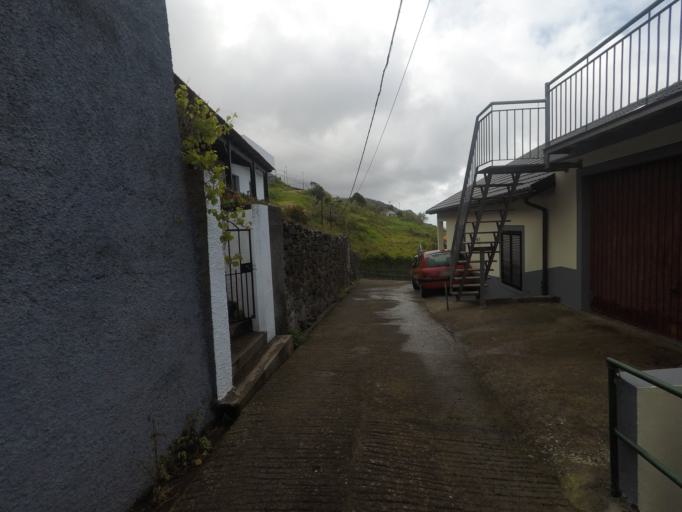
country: PT
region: Madeira
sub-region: Calheta
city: Faja da Ovelha
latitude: 32.7751
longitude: -17.2362
